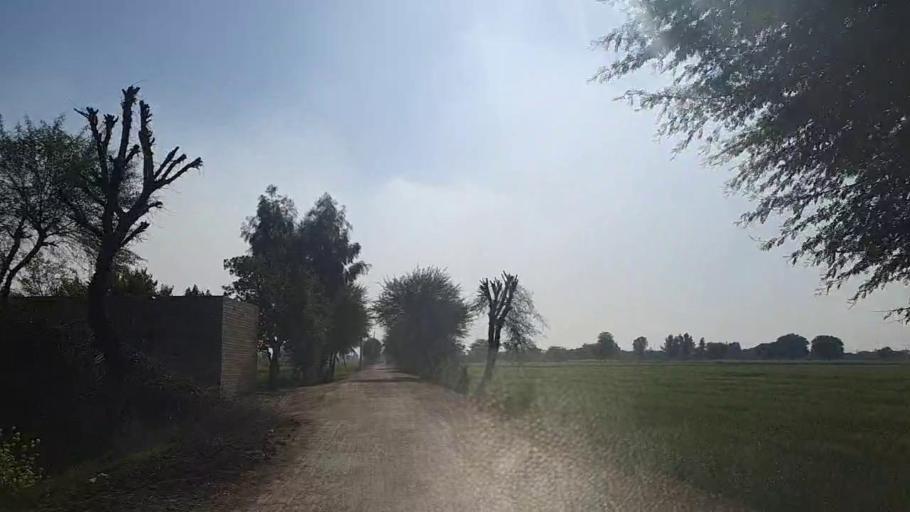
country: PK
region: Sindh
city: Shahpur Chakar
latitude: 26.1983
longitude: 68.6130
